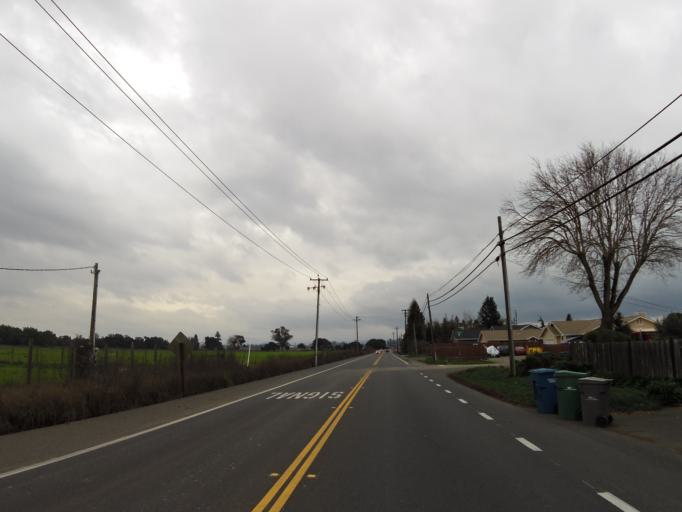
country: US
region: California
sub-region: Sonoma County
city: Penngrove
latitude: 38.3267
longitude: -122.6667
